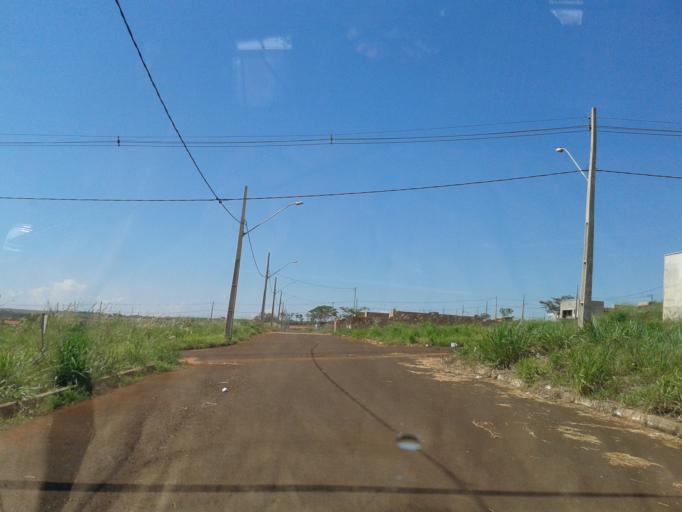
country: BR
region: Goias
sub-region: Itumbiara
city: Itumbiara
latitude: -18.4251
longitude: -49.1856
